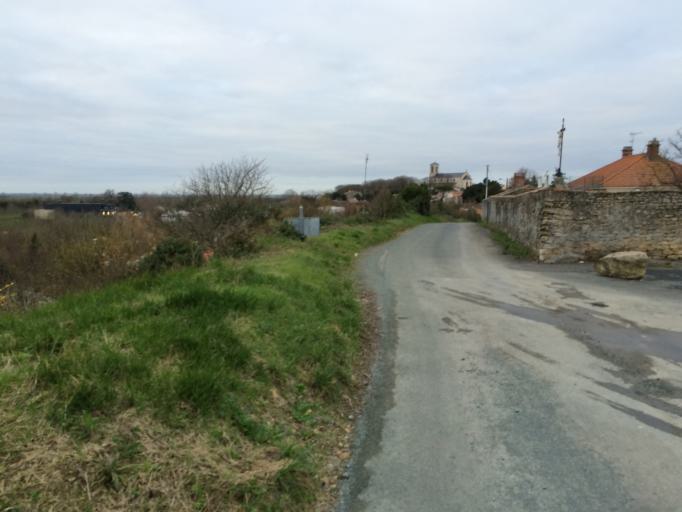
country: FR
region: Pays de la Loire
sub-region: Departement de la Vendee
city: Chaille-les-Marais
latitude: 46.3908
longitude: -1.0173
